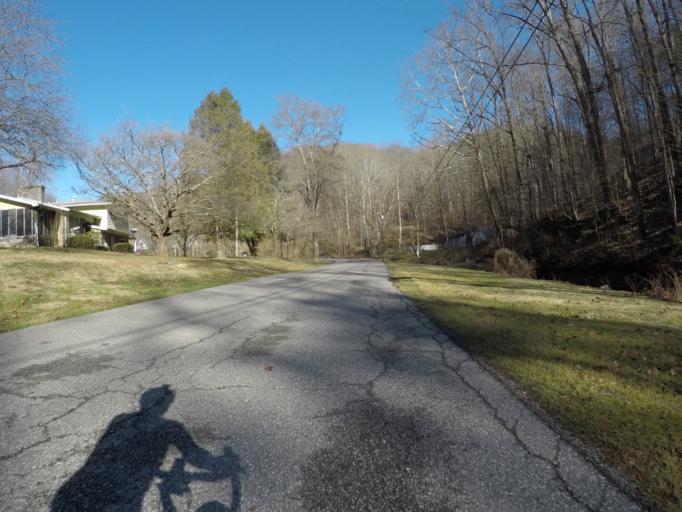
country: US
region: Kentucky
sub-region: Boyd County
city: Catlettsburg
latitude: 38.4189
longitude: -82.6391
